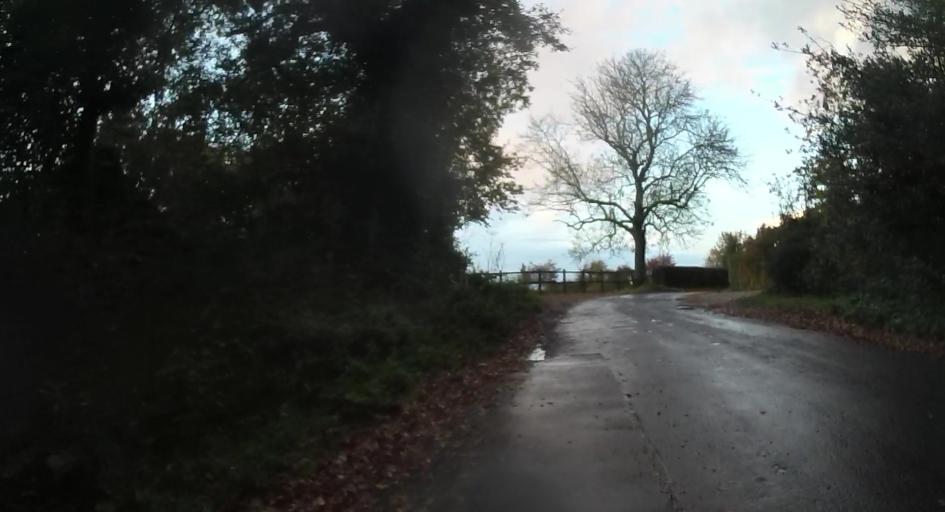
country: GB
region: England
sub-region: Hampshire
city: Long Sutton
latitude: 51.2010
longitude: -0.9403
